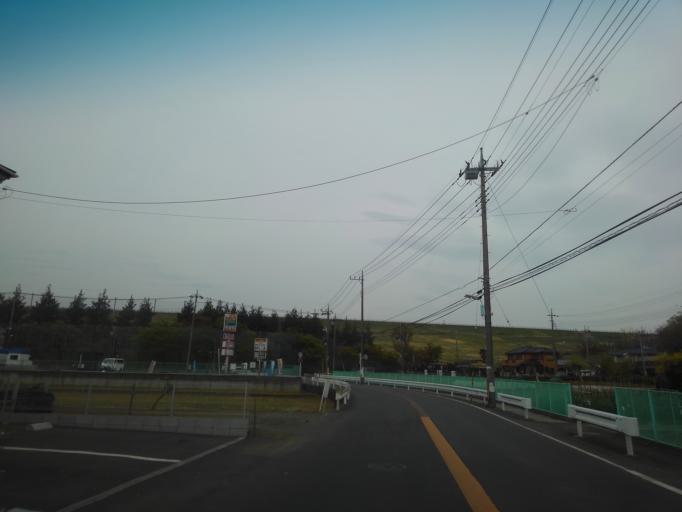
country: JP
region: Saitama
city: Tokorozawa
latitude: 35.7779
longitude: 139.4189
